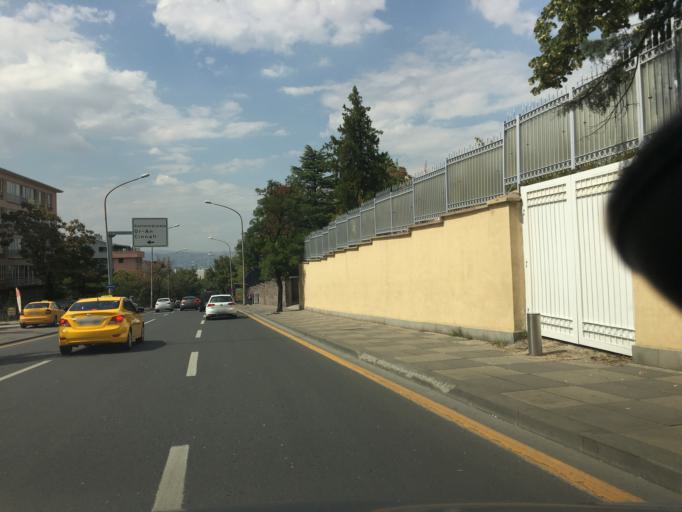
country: TR
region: Ankara
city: Cankaya
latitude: 39.8970
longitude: 32.8618
